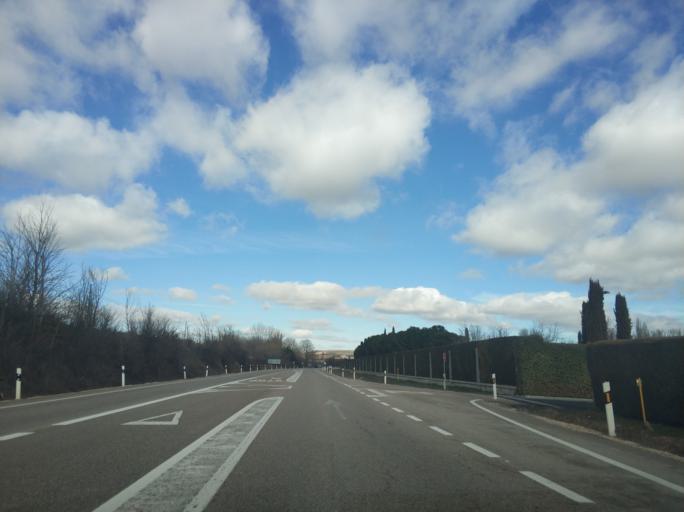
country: ES
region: Castille and Leon
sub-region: Provincia de Burgos
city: Sarracin
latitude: 42.2530
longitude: -3.6881
